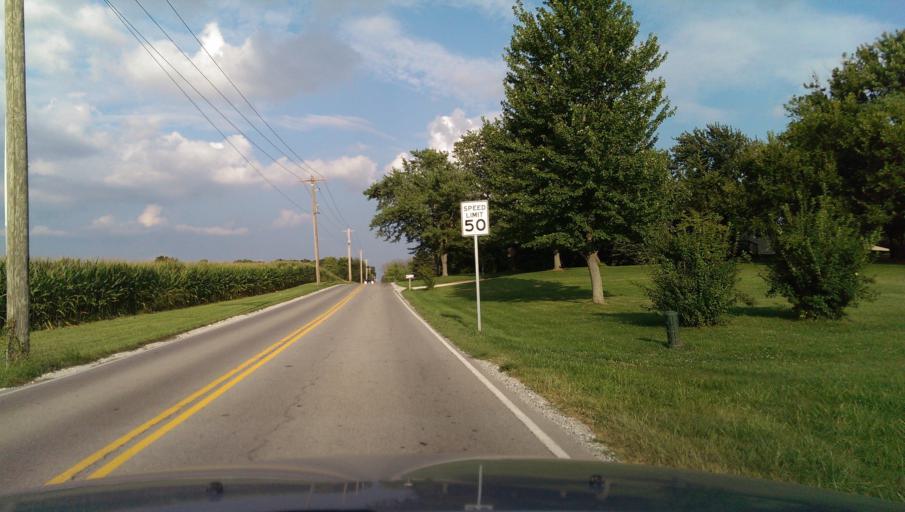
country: US
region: Indiana
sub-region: Hamilton County
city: Westfield
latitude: 40.0649
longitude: -86.1174
